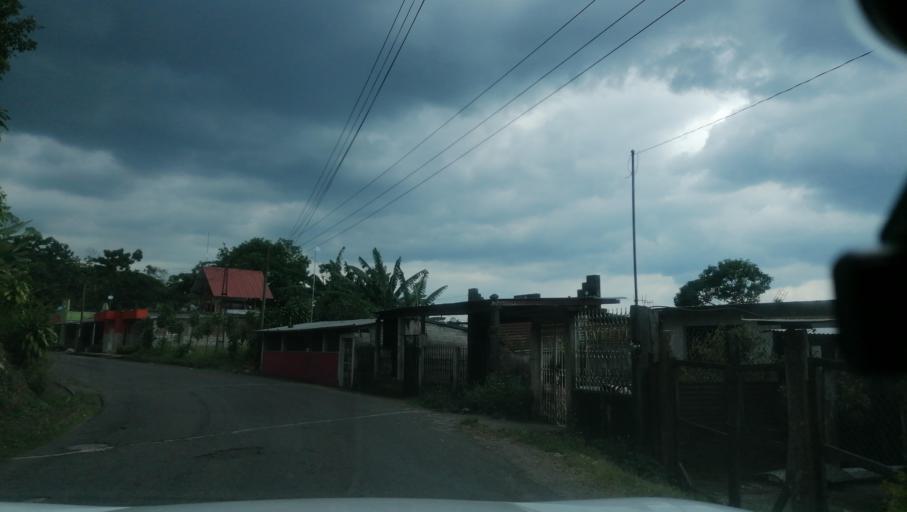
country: MX
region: Chiapas
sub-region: Cacahoatan
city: Benito Juarez
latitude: 15.0745
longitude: -92.1958
